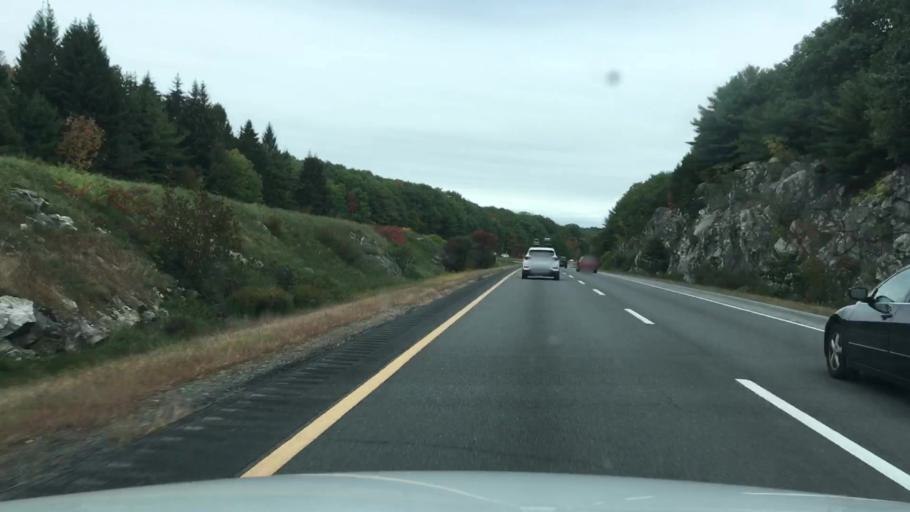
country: US
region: Maine
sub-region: Cumberland County
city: Falmouth
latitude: 43.7059
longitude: -70.2556
